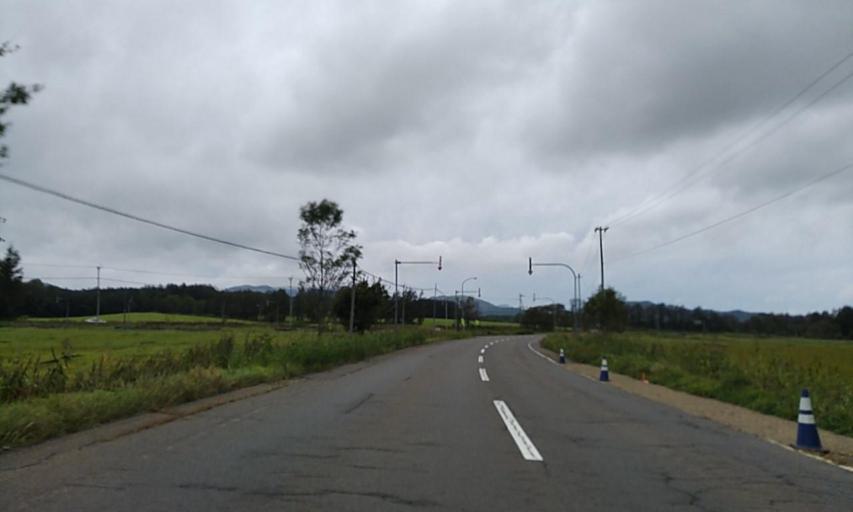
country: JP
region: Hokkaido
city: Bihoro
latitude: 43.5202
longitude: 144.4158
